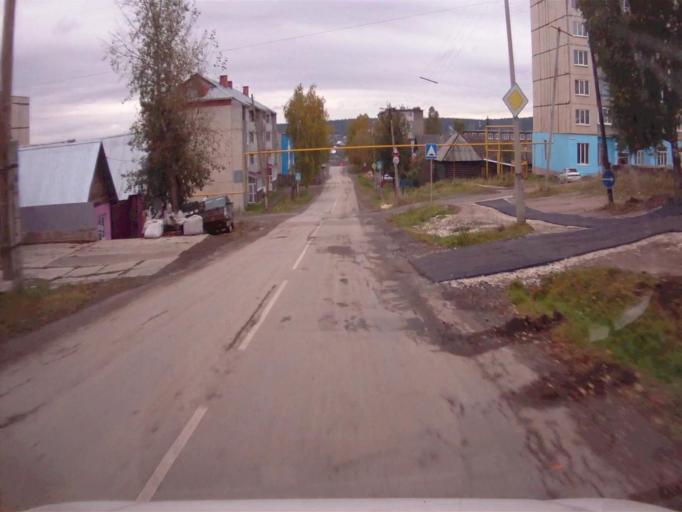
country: RU
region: Chelyabinsk
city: Nyazepetrovsk
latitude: 56.0570
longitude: 59.6074
